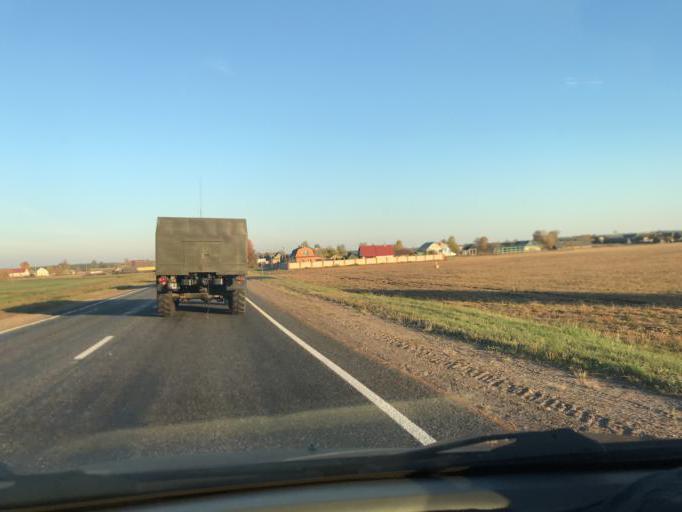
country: BY
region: Minsk
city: Staryya Darohi
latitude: 53.0469
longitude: 28.0992
